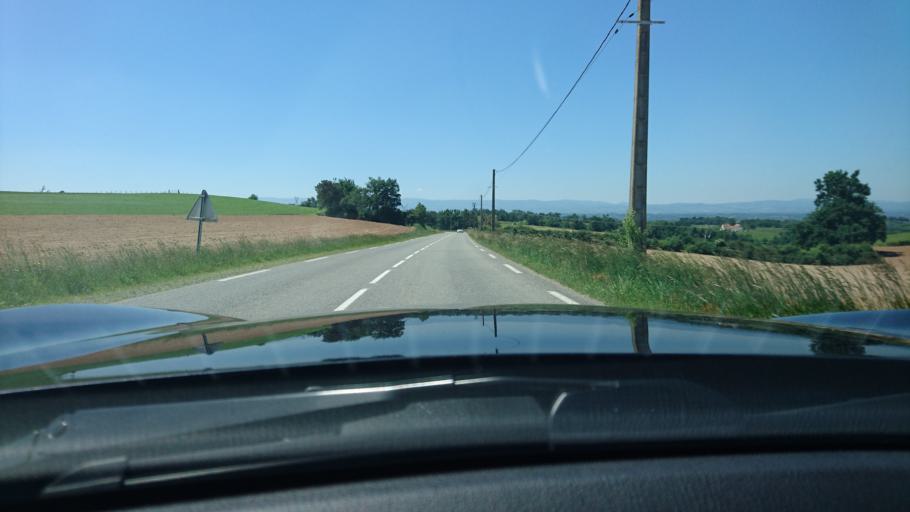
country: FR
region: Rhone-Alpes
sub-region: Departement de la Loire
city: Rozier-en-Donzy
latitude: 45.7811
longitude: 4.2796
